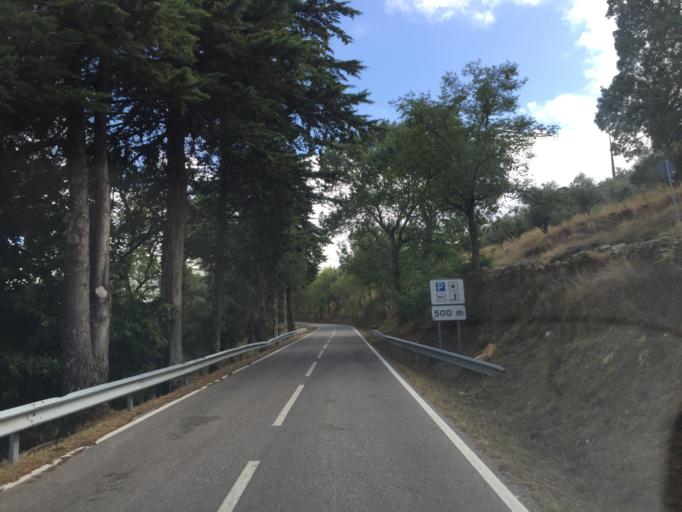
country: PT
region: Portalegre
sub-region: Marvao
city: Marvao
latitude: 39.3961
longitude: -7.3756
